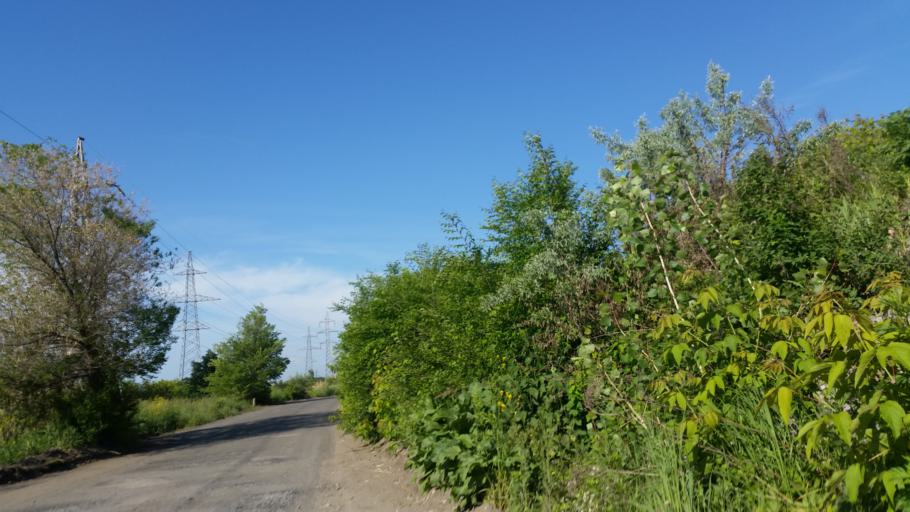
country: RU
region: Ulyanovsk
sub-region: Ulyanovskiy Rayon
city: Ulyanovsk
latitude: 54.3064
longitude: 48.4064
